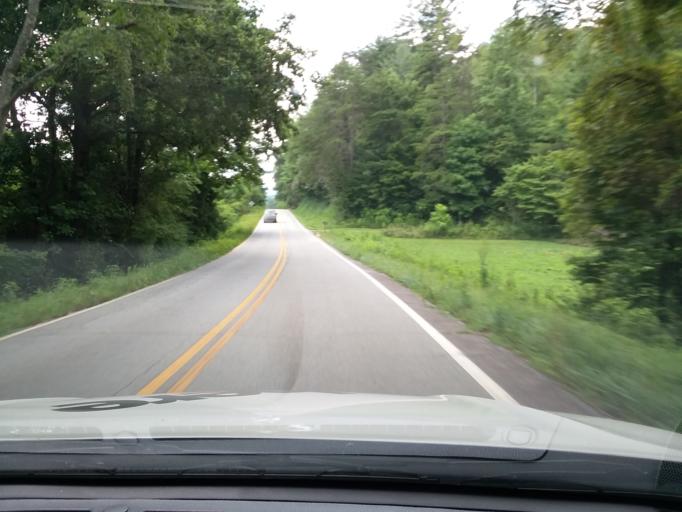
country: US
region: Georgia
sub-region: Rabun County
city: Mountain City
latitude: 34.8989
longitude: -83.2805
